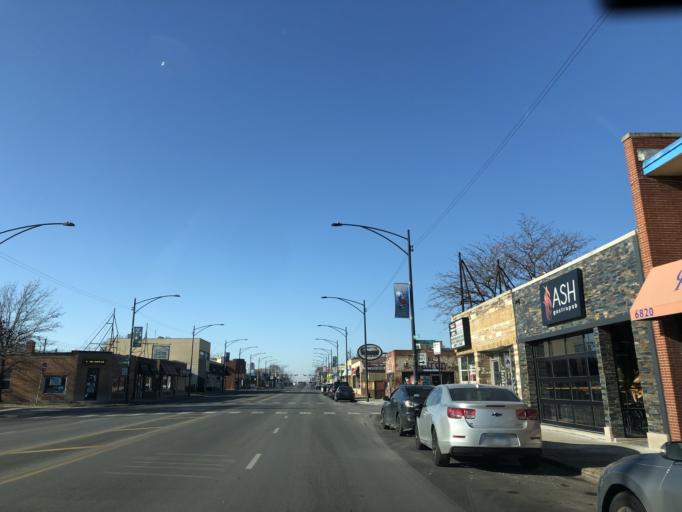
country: US
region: Illinois
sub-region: Cook County
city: Summit
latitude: 41.7922
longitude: -87.7923
